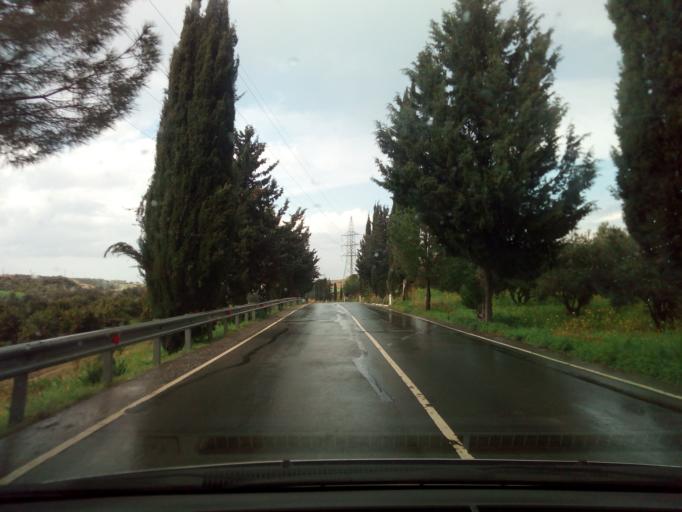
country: CY
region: Pafos
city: Polis
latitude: 35.0230
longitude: 32.4447
